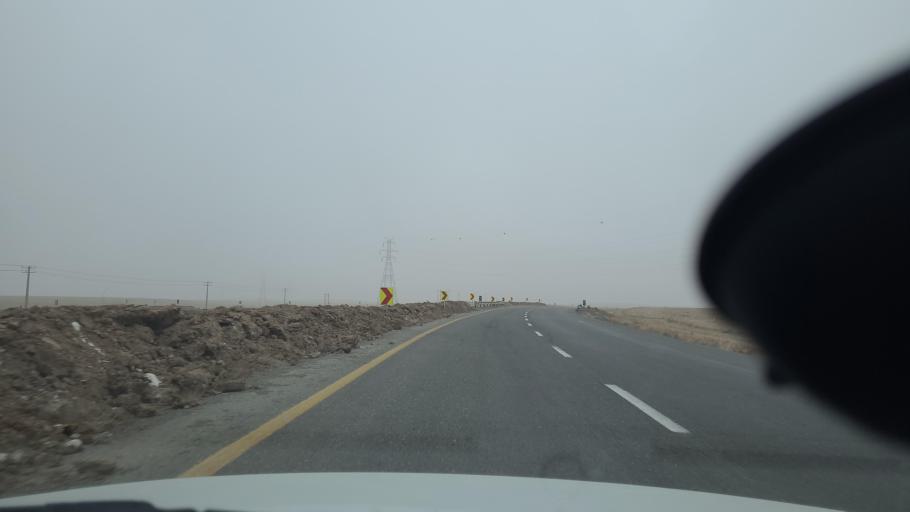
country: IR
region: Razavi Khorasan
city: Fariman
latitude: 35.8679
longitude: 59.7621
